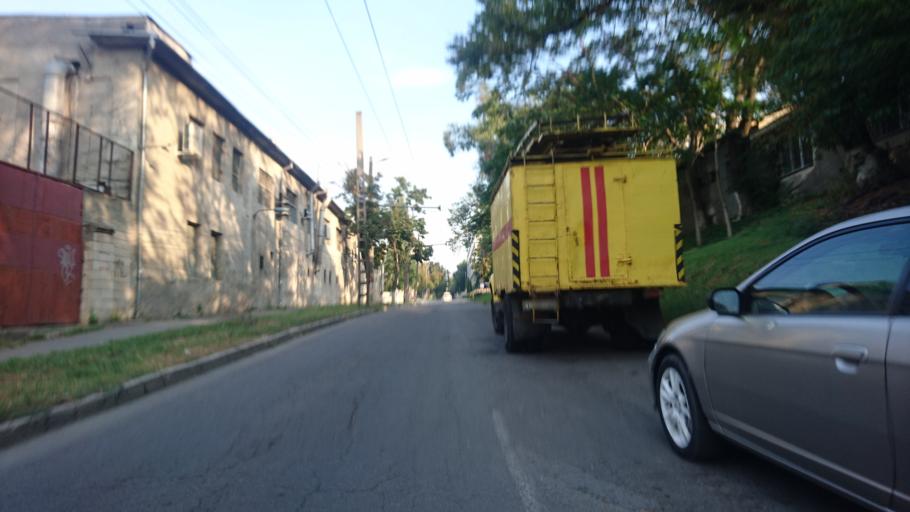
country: MD
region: Chisinau
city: Chisinau
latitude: 47.0343
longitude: 28.8223
